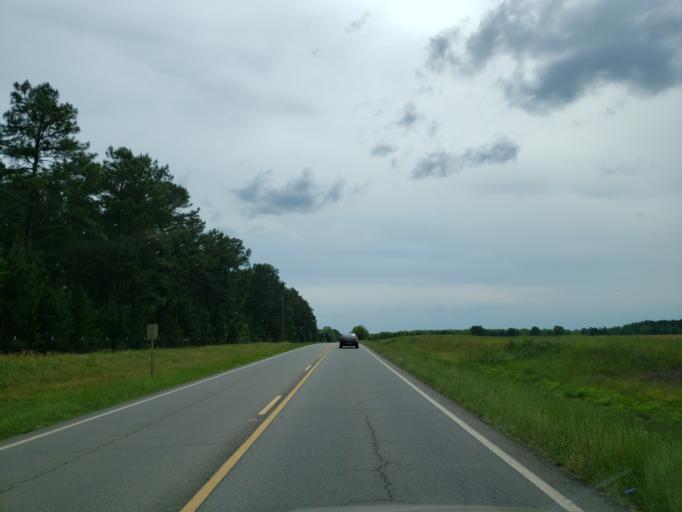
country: US
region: Georgia
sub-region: Houston County
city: Perry
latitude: 32.4257
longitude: -83.8292
